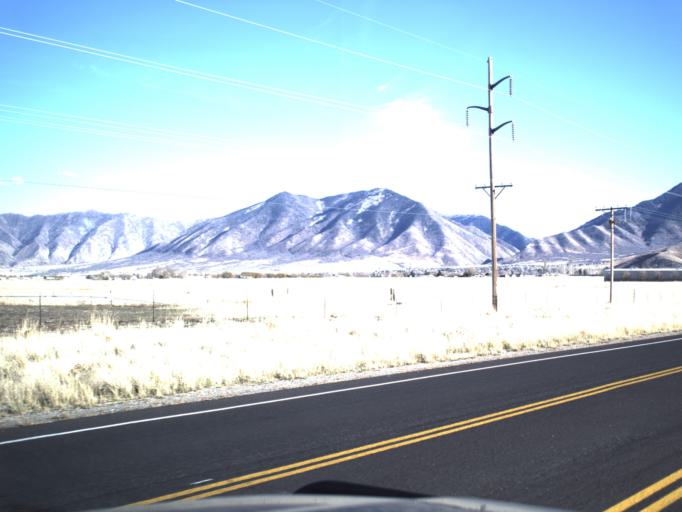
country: US
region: Utah
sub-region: Tooele County
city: Tooele
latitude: 40.5411
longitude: -112.3356
